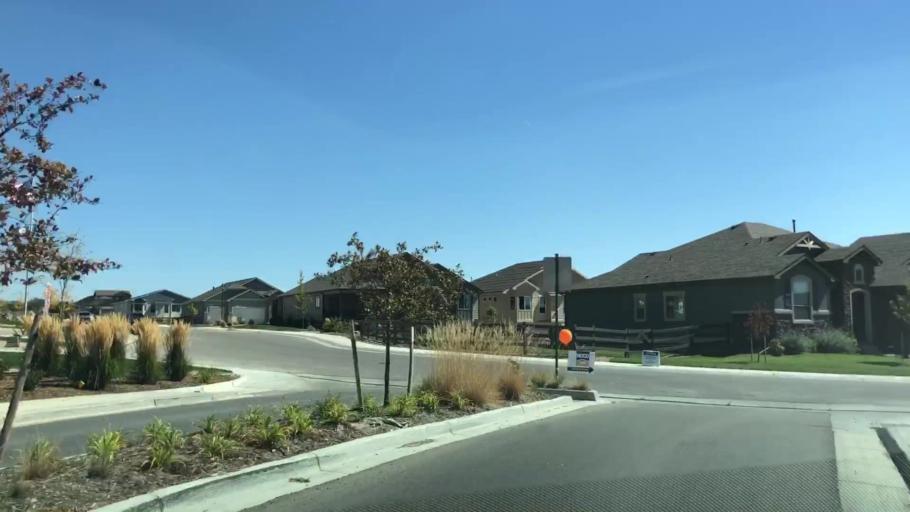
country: US
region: Colorado
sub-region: Weld County
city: Johnstown
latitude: 40.3995
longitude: -104.9718
